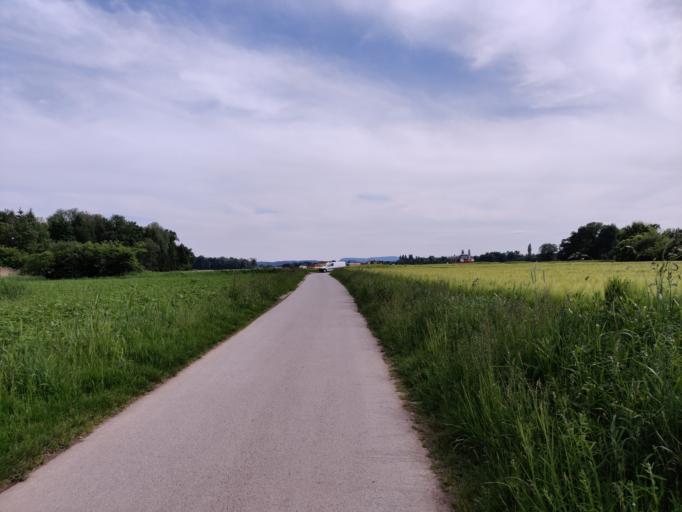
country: AT
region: Styria
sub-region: Politischer Bezirk Graz-Umgebung
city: Gossendorf
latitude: 46.9809
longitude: 15.4720
